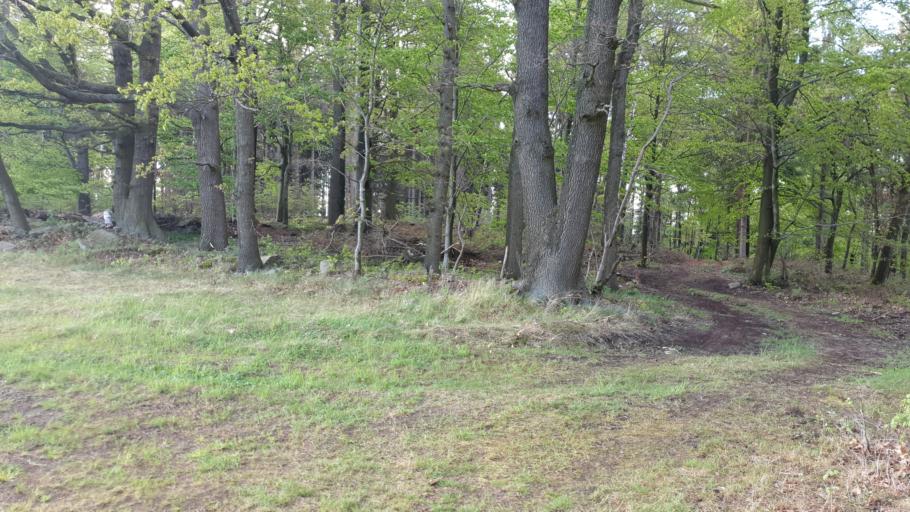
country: DE
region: Saxony
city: Mulda
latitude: 50.8296
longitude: 13.3747
